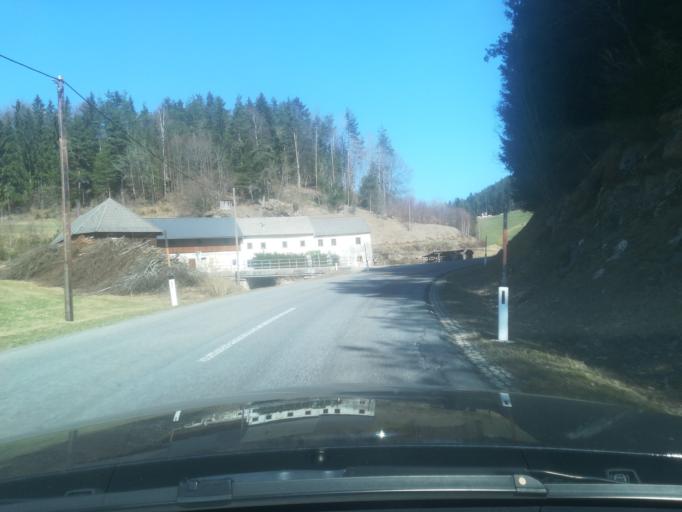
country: AT
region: Lower Austria
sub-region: Politischer Bezirk Zwettl
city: Langschlag
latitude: 48.4681
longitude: 14.7952
